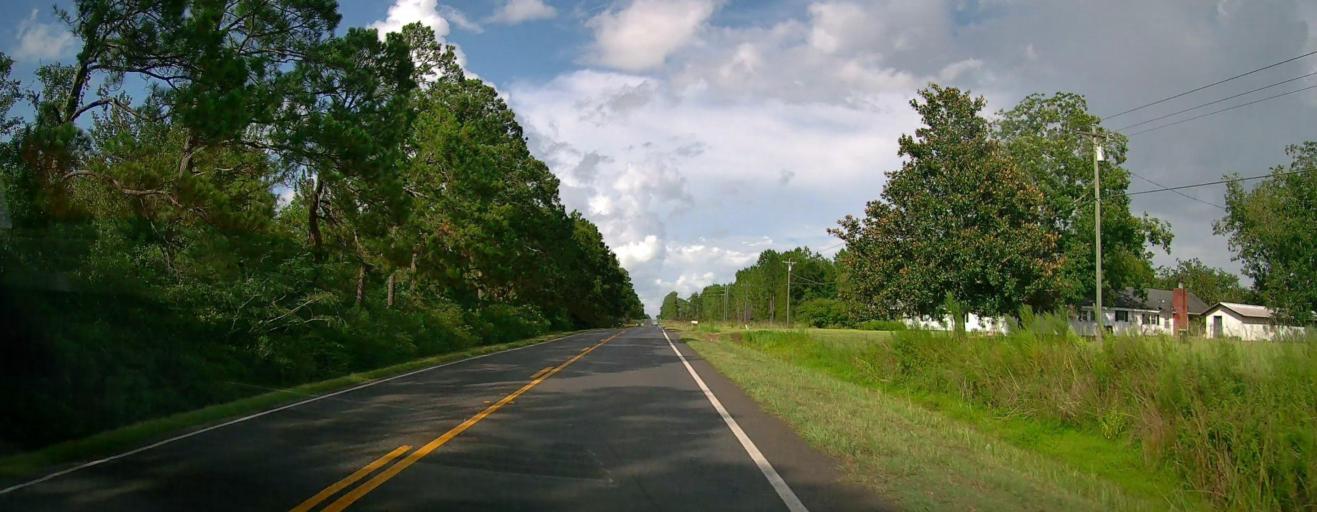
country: US
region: Georgia
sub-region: Coffee County
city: Douglas
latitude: 31.4718
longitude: -82.8767
